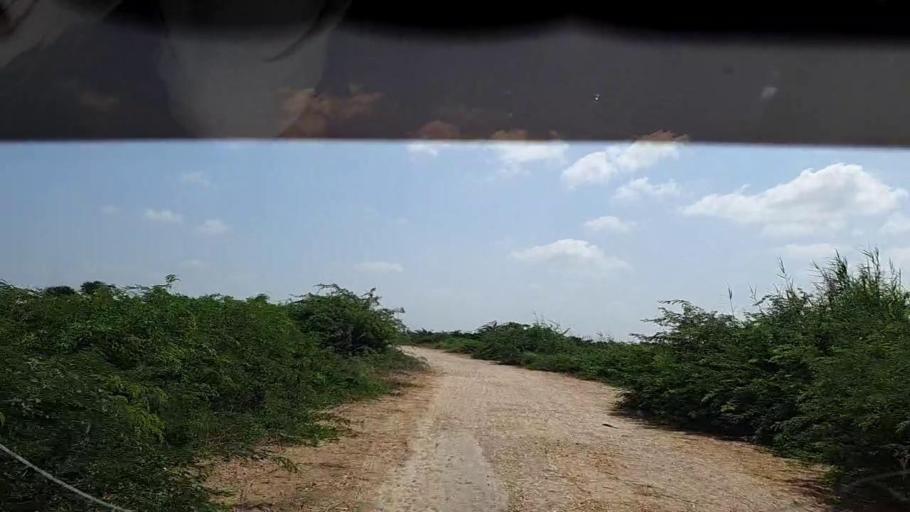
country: PK
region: Sindh
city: Kadhan
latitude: 24.6038
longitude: 68.9788
